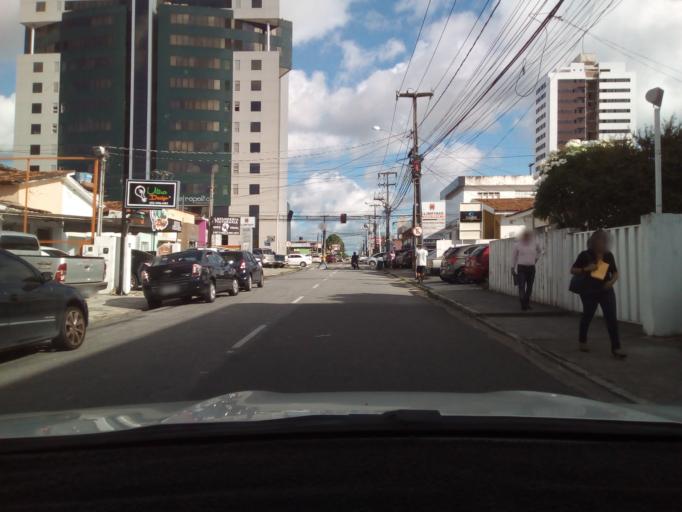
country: BR
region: Paraiba
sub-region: Joao Pessoa
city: Joao Pessoa
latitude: -7.1205
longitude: -34.8553
